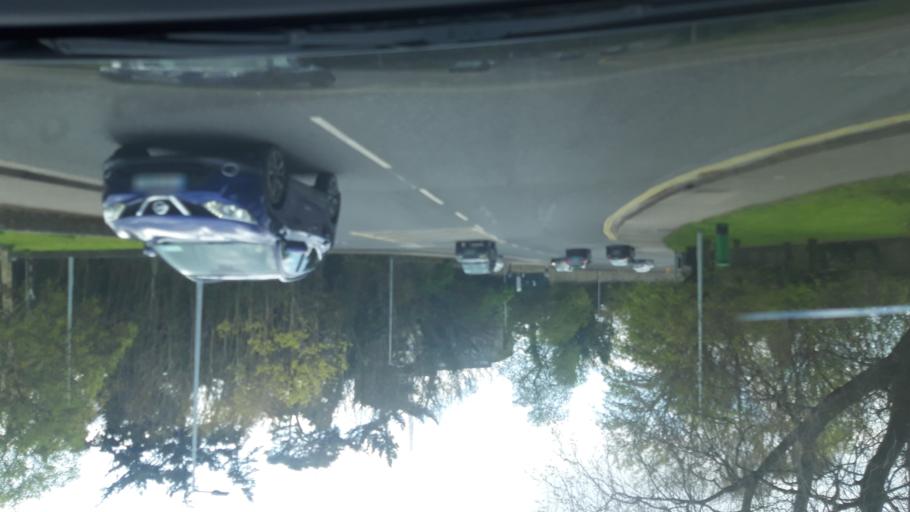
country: IE
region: Leinster
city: Rathgar
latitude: 53.3057
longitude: -6.2666
